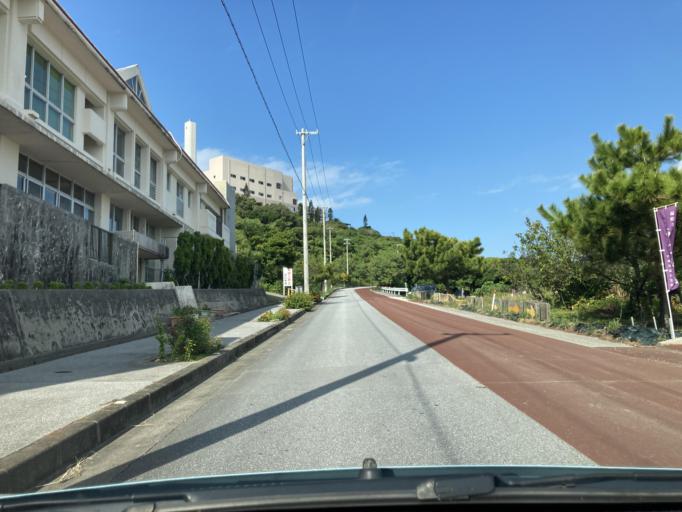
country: JP
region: Okinawa
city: Ginowan
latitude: 26.2769
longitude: 127.7969
